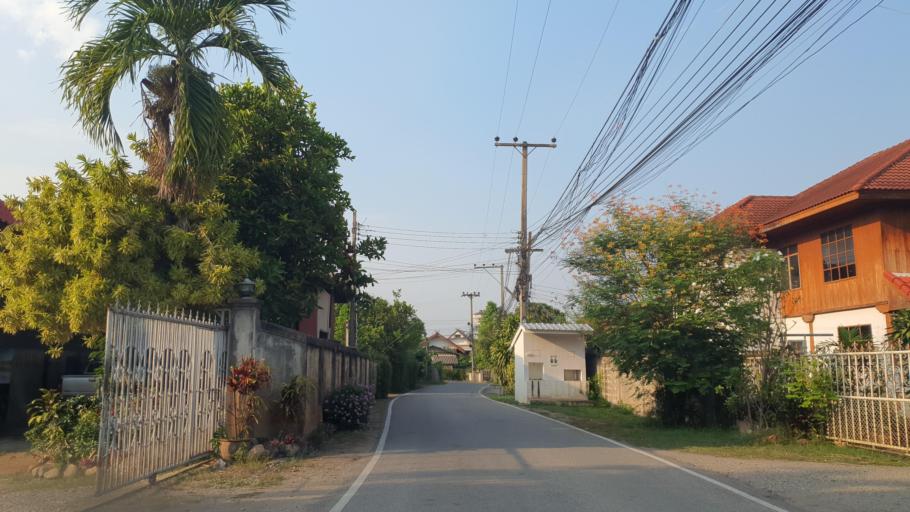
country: TH
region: Chiang Mai
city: San Pa Tong
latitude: 18.6383
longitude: 98.8701
